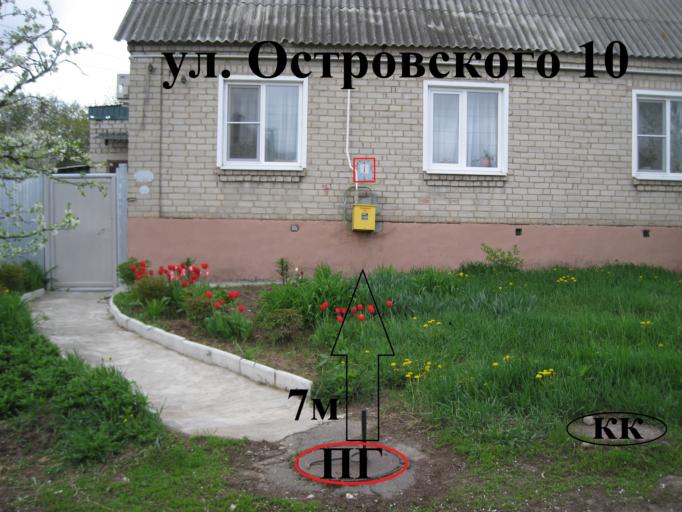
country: RU
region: Voronezj
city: Voronezh
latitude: 51.6440
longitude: 39.1874
